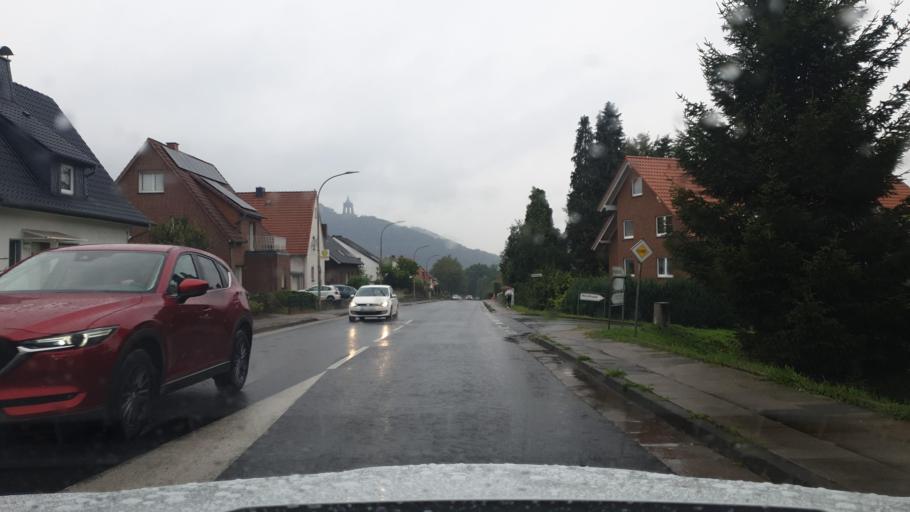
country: DE
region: North Rhine-Westphalia
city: Porta Westfalica
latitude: 52.2302
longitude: 8.9143
